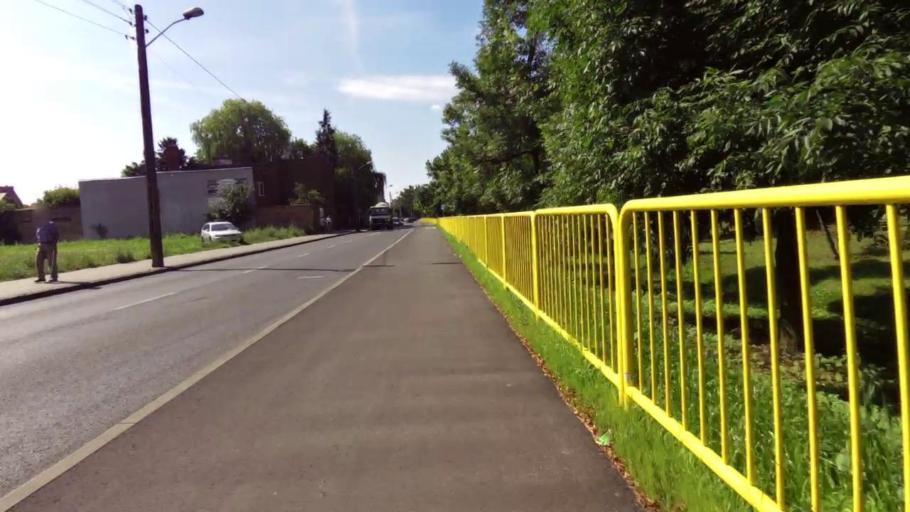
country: PL
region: West Pomeranian Voivodeship
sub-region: Powiat stargardzki
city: Stargard Szczecinski
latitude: 53.3393
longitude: 15.0506
